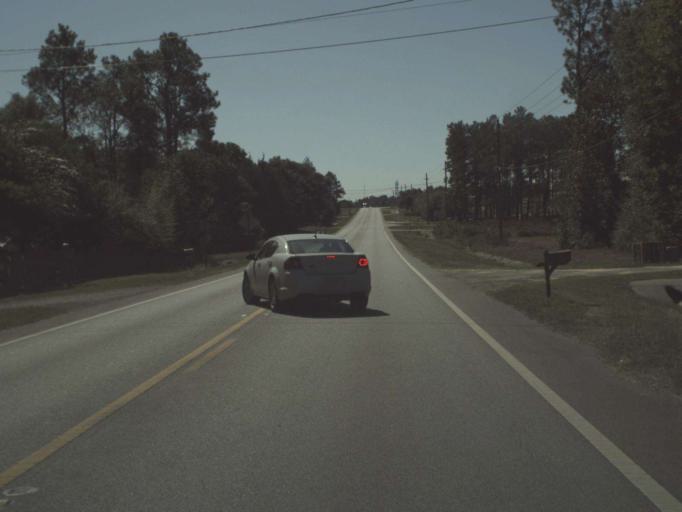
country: US
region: Florida
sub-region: Walton County
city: DeFuniak Springs
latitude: 30.7476
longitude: -86.1145
